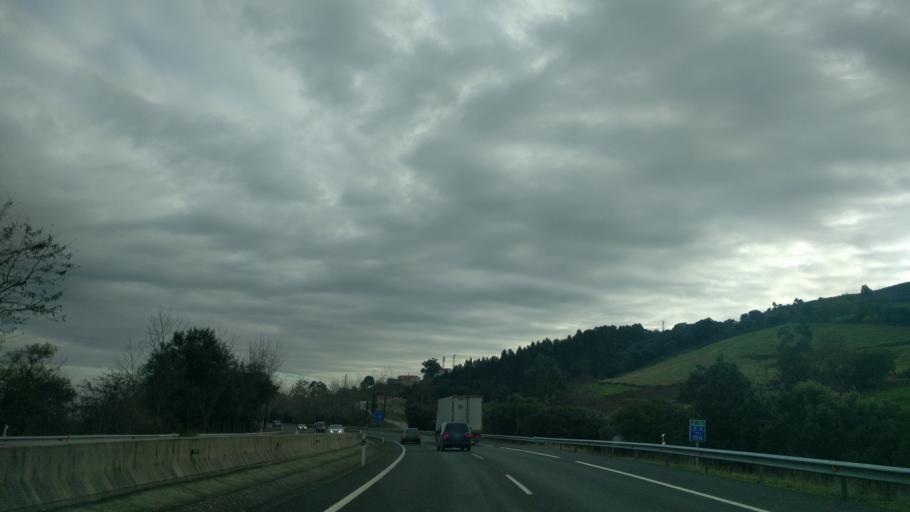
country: ES
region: Cantabria
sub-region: Provincia de Cantabria
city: Castro-Urdiales
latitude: 43.3980
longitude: -3.2654
